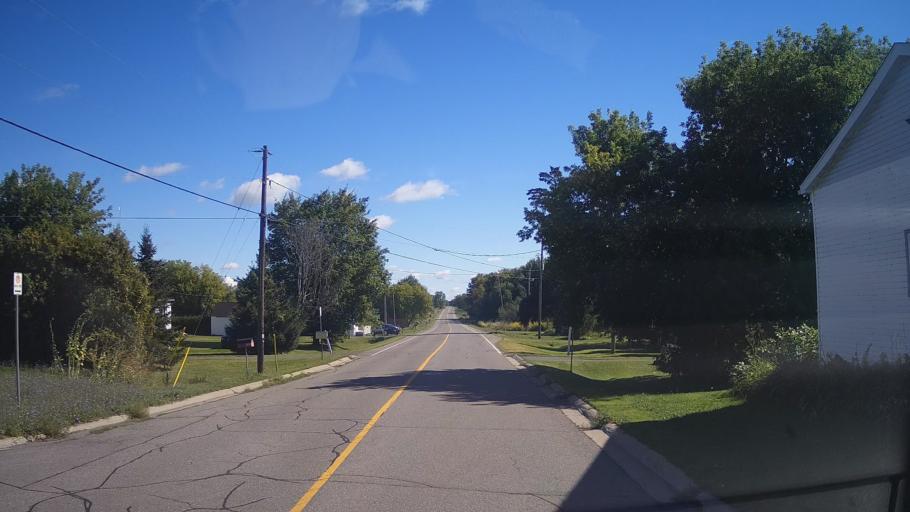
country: US
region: New York
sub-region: St. Lawrence County
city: Ogdensburg
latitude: 44.9406
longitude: -75.3065
